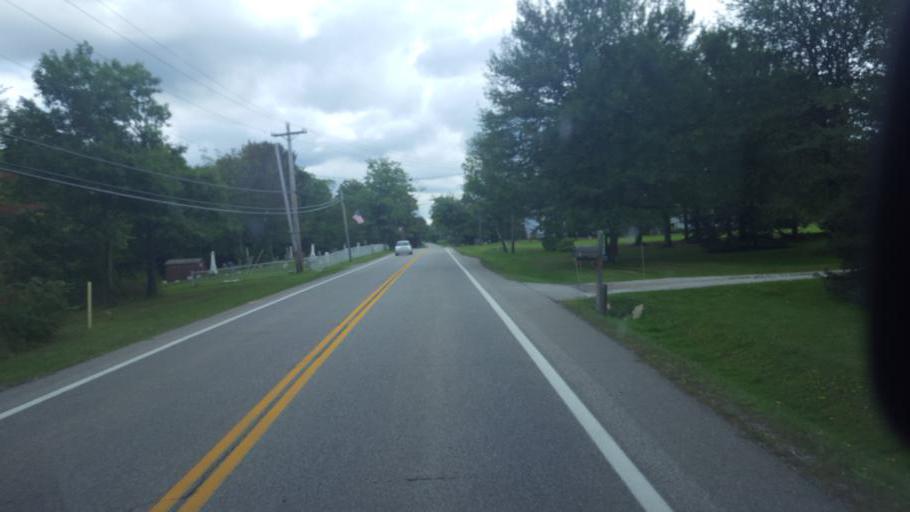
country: US
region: Ohio
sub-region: Geauga County
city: Chardon
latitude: 41.6610
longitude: -81.1367
